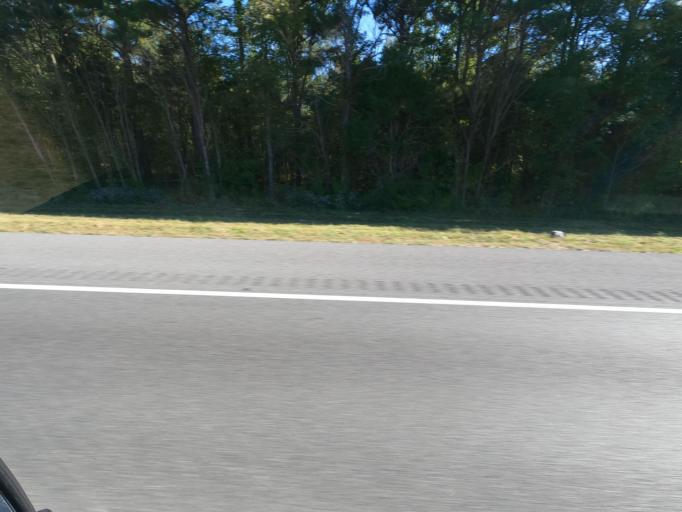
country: US
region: Tennessee
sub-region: Rutherford County
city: Plainview
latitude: 35.7329
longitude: -86.3288
